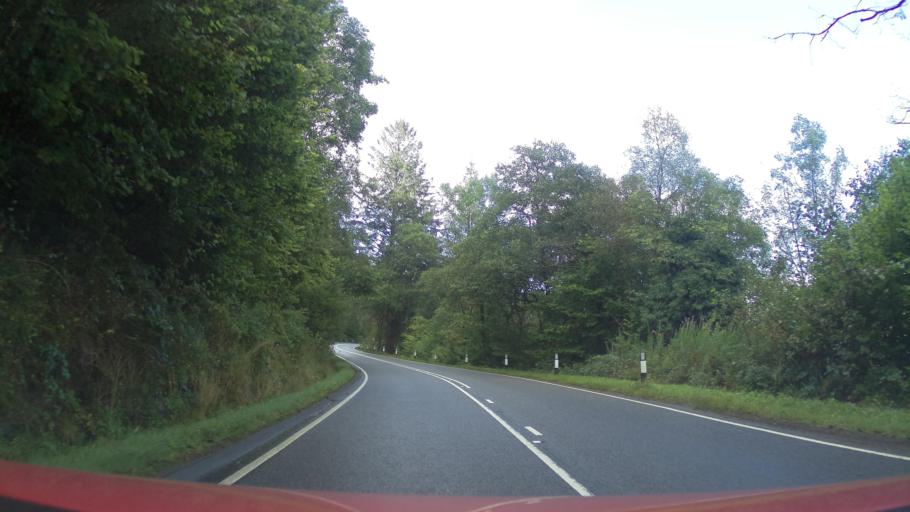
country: GB
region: Scotland
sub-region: Highland
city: Fort William
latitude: 56.7531
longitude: -5.1917
